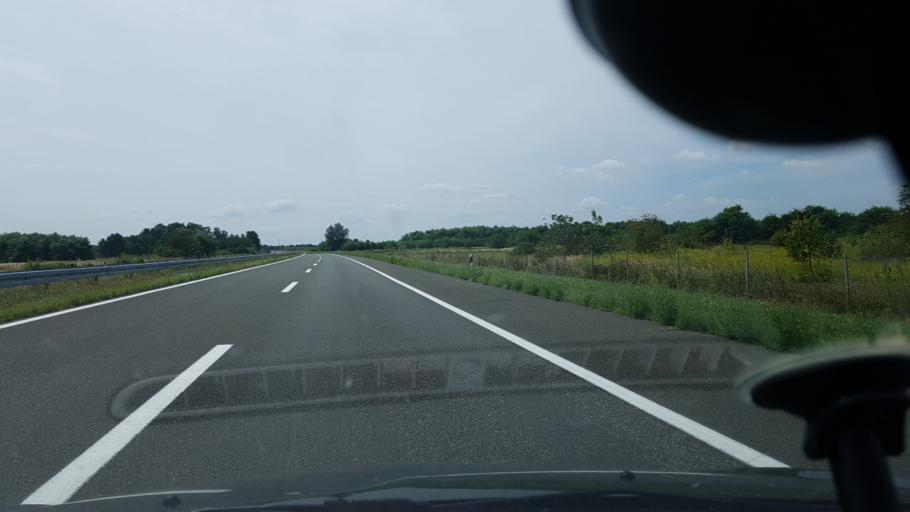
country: HR
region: Medimurska
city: Palovec
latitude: 46.3964
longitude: 16.5678
